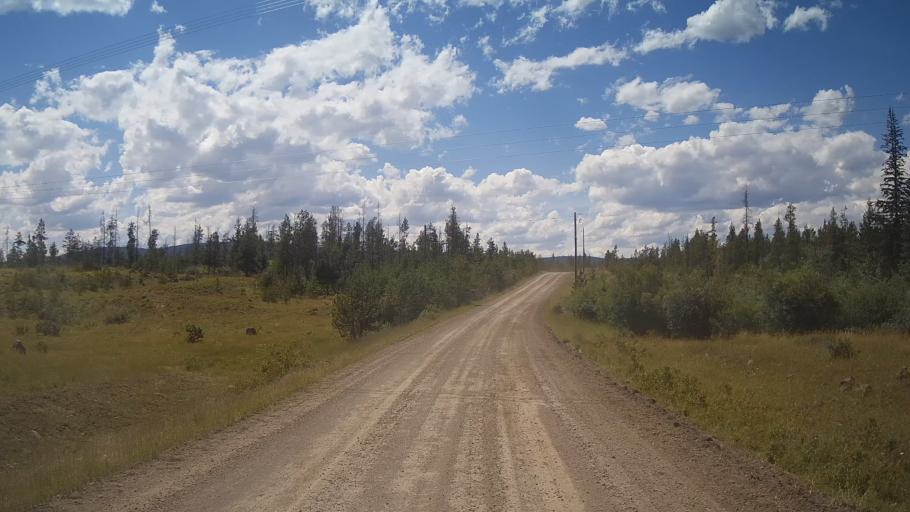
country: CA
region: British Columbia
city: Lillooet
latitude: 51.3361
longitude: -121.9639
